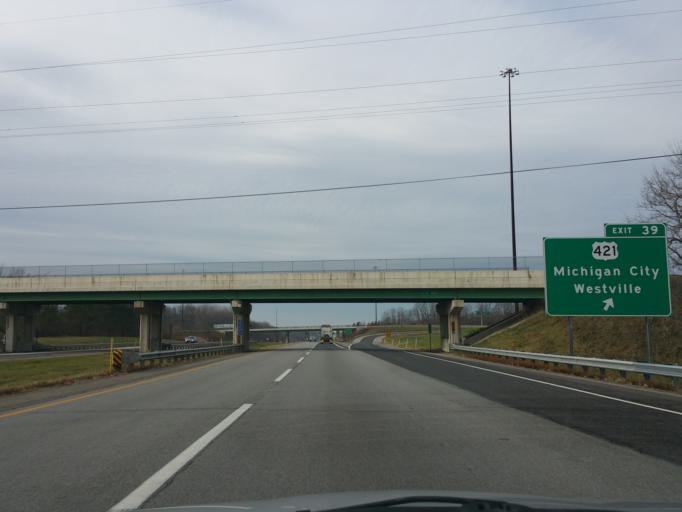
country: US
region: Indiana
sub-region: LaPorte County
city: Westville
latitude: 41.5909
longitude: -86.8963
